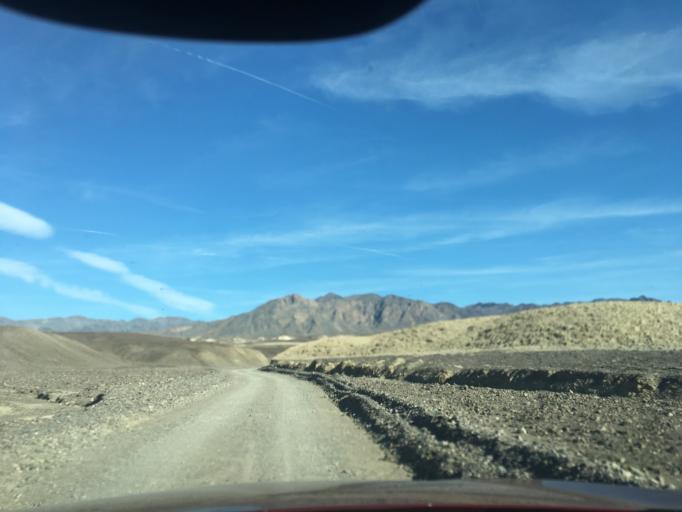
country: US
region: Nevada
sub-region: Nye County
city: Beatty
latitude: 36.4891
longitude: -116.8737
